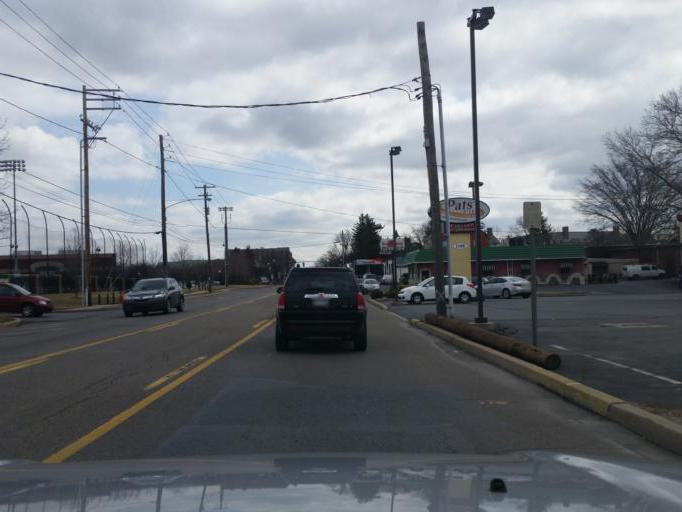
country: US
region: Pennsylvania
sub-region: Lancaster County
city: Lancaster
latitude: 40.0528
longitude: -76.3235
